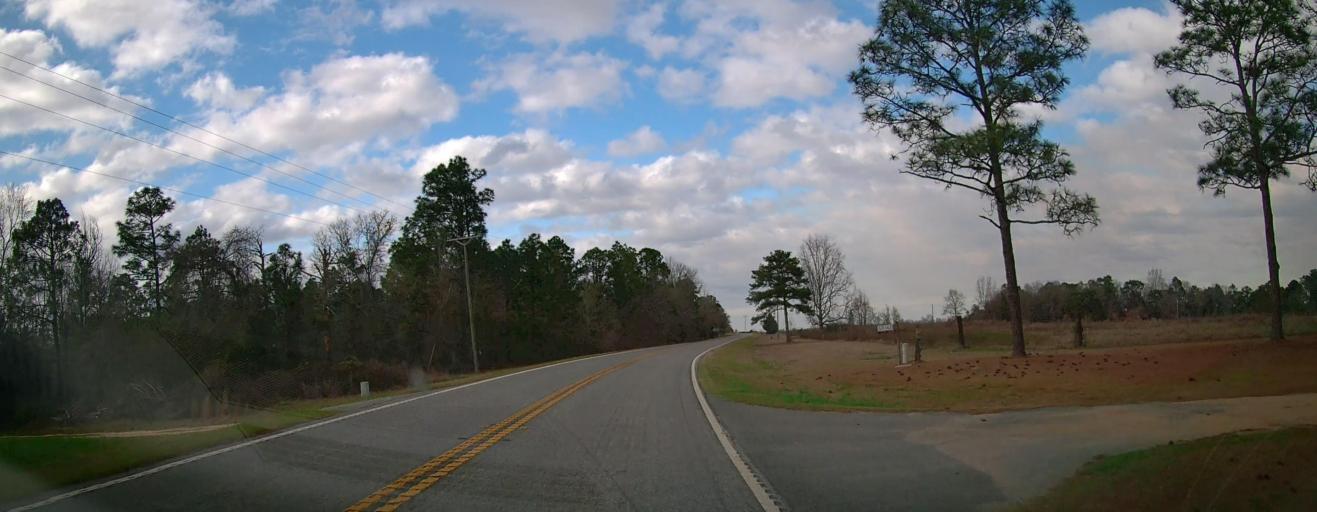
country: US
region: Georgia
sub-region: Marion County
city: Buena Vista
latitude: 32.4441
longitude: -84.4401
